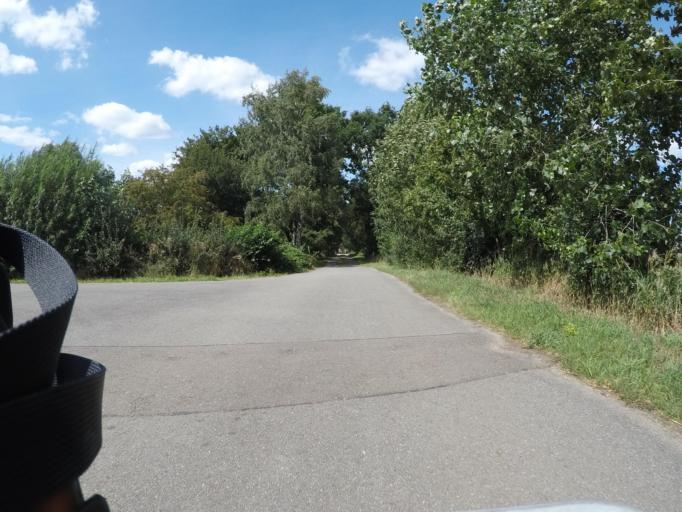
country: DE
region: Lower Saxony
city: Stelle
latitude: 53.4501
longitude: 10.1272
